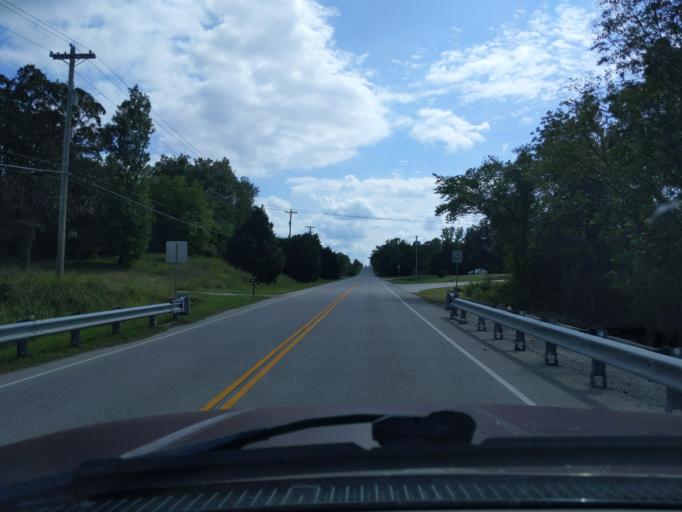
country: US
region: Oklahoma
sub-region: Tulsa County
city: Oakhurst
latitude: 36.0599
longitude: -96.0117
